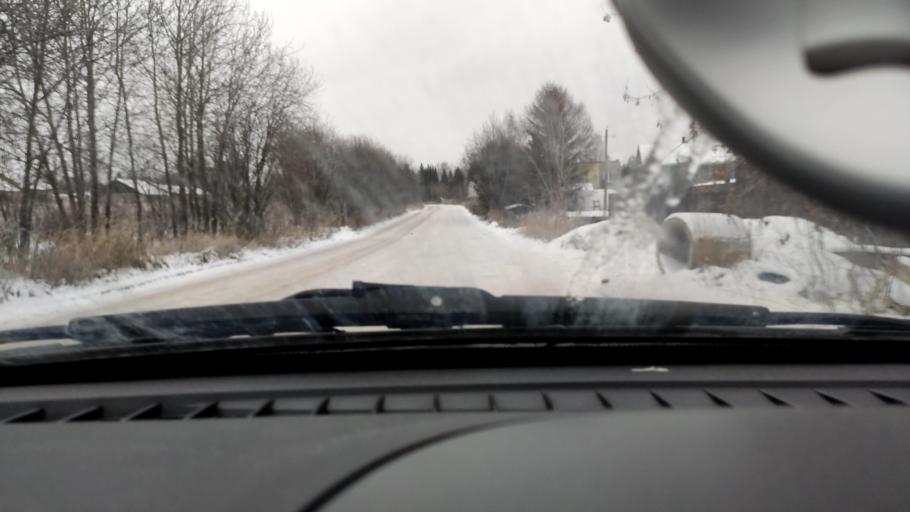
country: RU
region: Perm
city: Polazna
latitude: 58.1774
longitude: 56.4085
